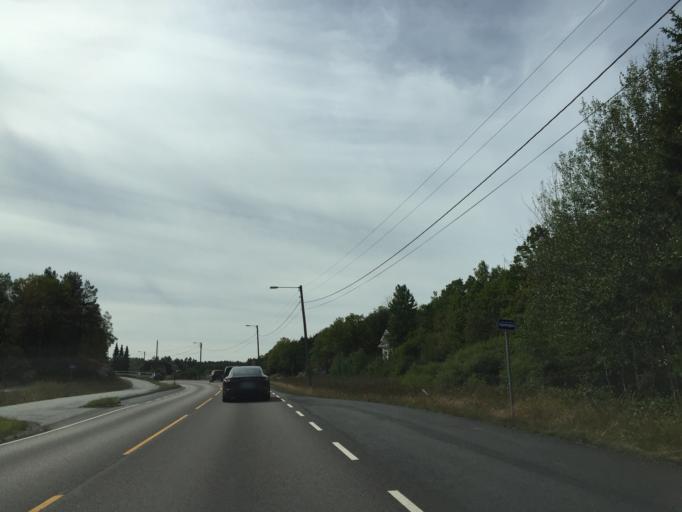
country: NO
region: Ostfold
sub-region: Fredrikstad
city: Fredrikstad
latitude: 59.1641
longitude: 10.9287
